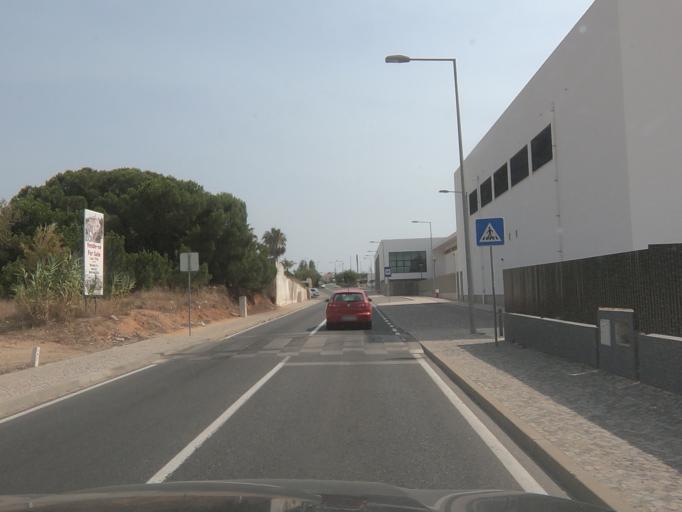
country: PT
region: Faro
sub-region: Loule
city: Quarteira
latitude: 37.0760
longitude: -8.0784
